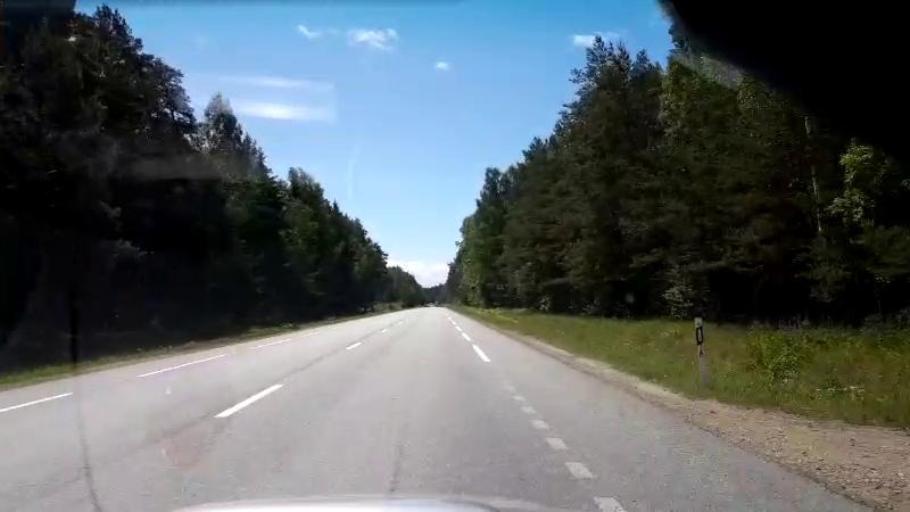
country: LV
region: Saulkrastu
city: Saulkrasti
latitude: 57.4574
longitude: 24.4318
